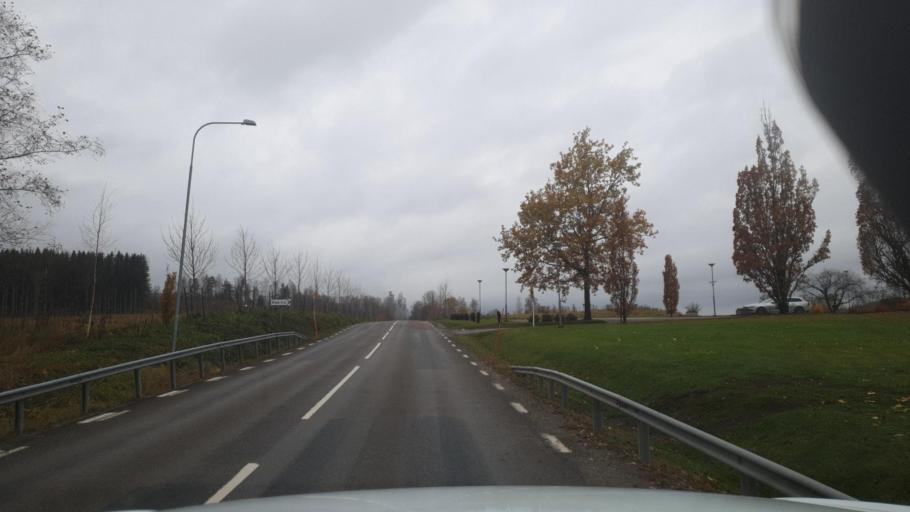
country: SE
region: Vaermland
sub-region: Arvika Kommun
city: Arvika
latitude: 59.6436
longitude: 12.4744
